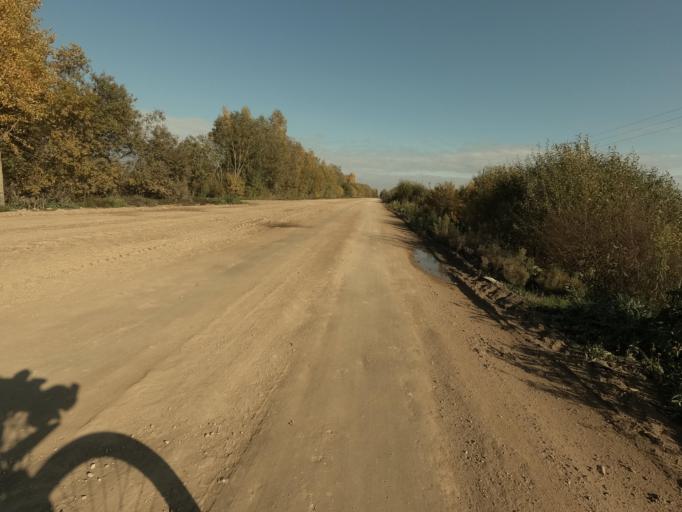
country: RU
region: Novgorod
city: Batetskiy
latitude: 58.8213
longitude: 30.7039
